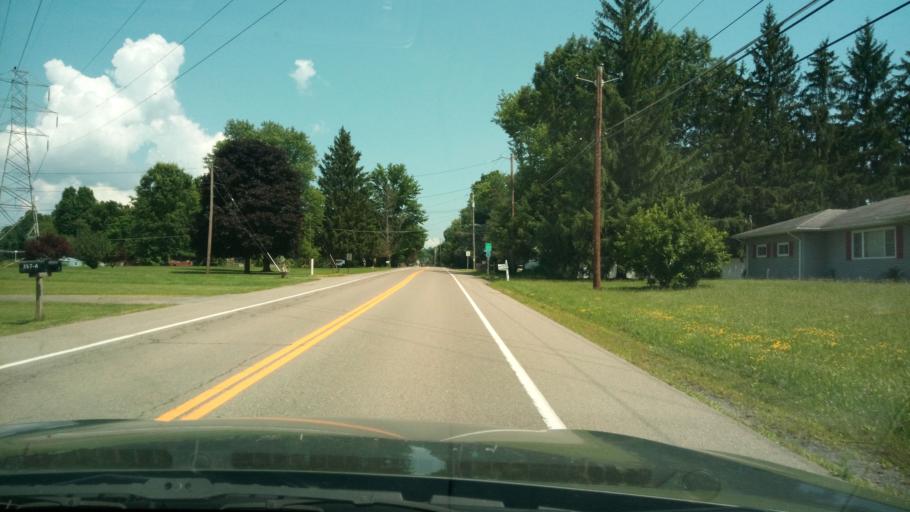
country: US
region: New York
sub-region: Chemung County
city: Horseheads North
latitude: 42.1994
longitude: -76.8121
